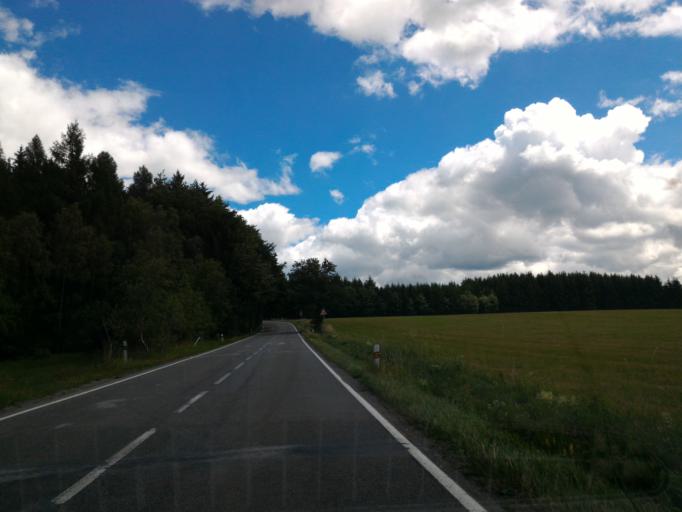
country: CZ
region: Vysocina
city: Bohdalov
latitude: 49.4603
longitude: 15.8206
